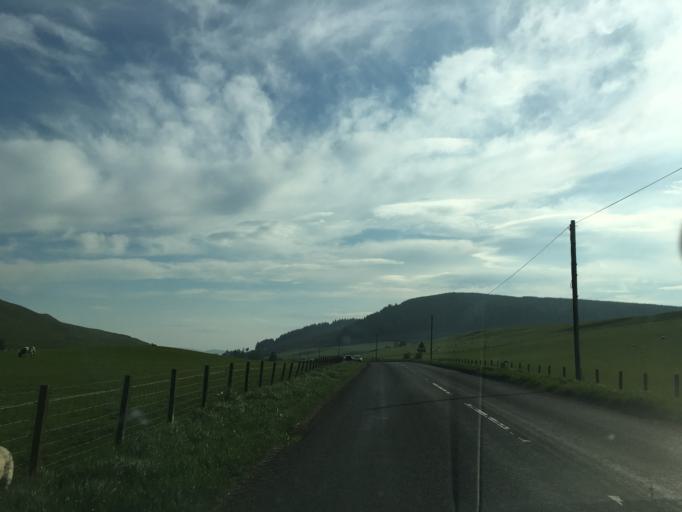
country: GB
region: Scotland
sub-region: The Scottish Borders
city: West Linton
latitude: 55.6723
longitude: -3.4155
